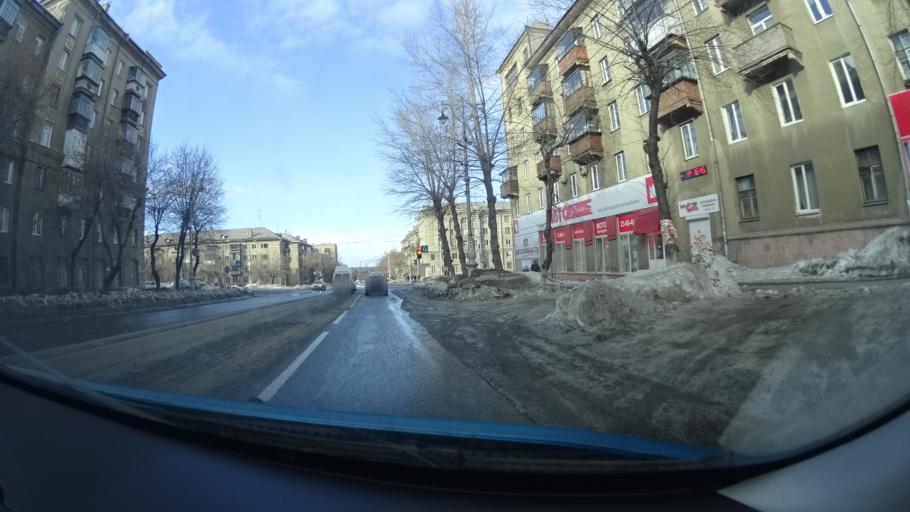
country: RU
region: Chelyabinsk
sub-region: Gorod Magnitogorsk
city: Magnitogorsk
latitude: 53.4337
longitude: 58.9837
